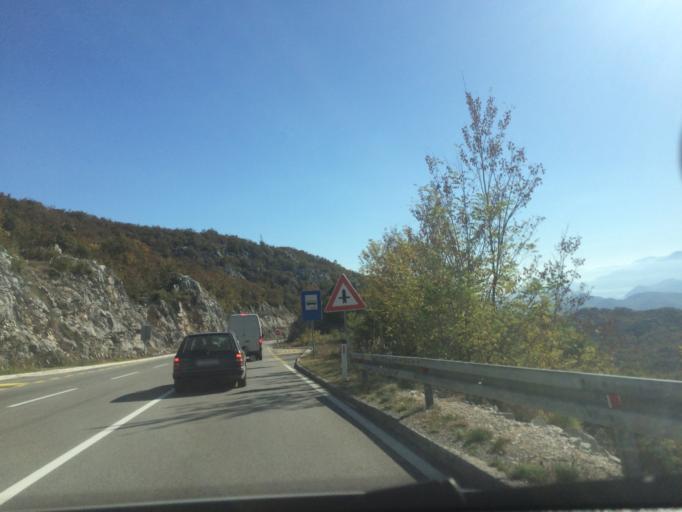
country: ME
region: Cetinje
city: Cetinje
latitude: 42.3788
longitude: 19.0267
